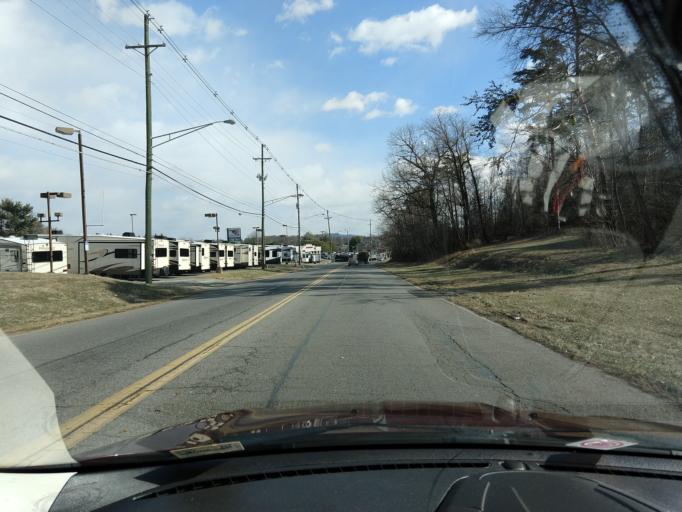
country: US
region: Virginia
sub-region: City of Salem
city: Salem
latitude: 37.2968
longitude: -80.0377
